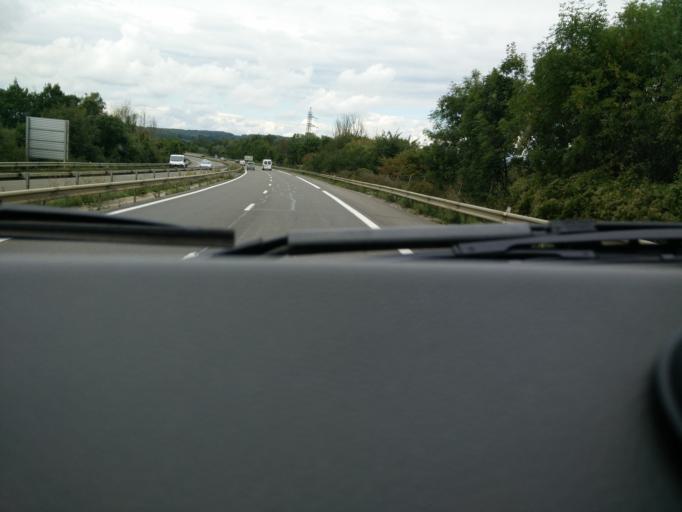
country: FR
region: Champagne-Ardenne
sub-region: Departement des Ardennes
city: Donchery
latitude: 49.7047
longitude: 4.9026
